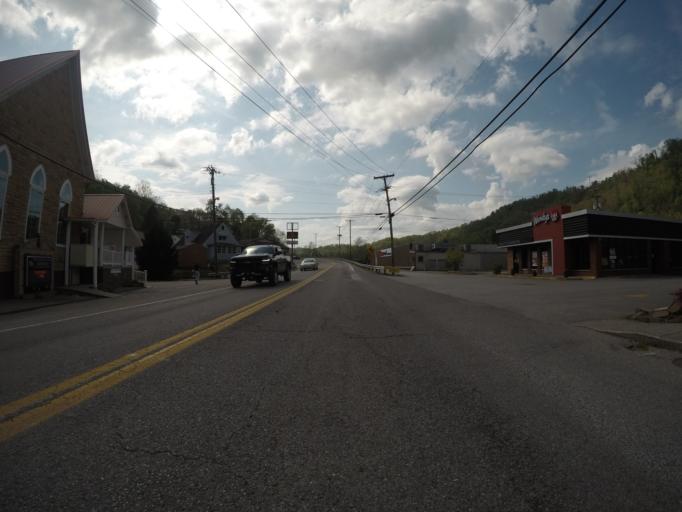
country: US
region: West Virginia
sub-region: Boone County
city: Madison
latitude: 38.0782
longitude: -81.8322
